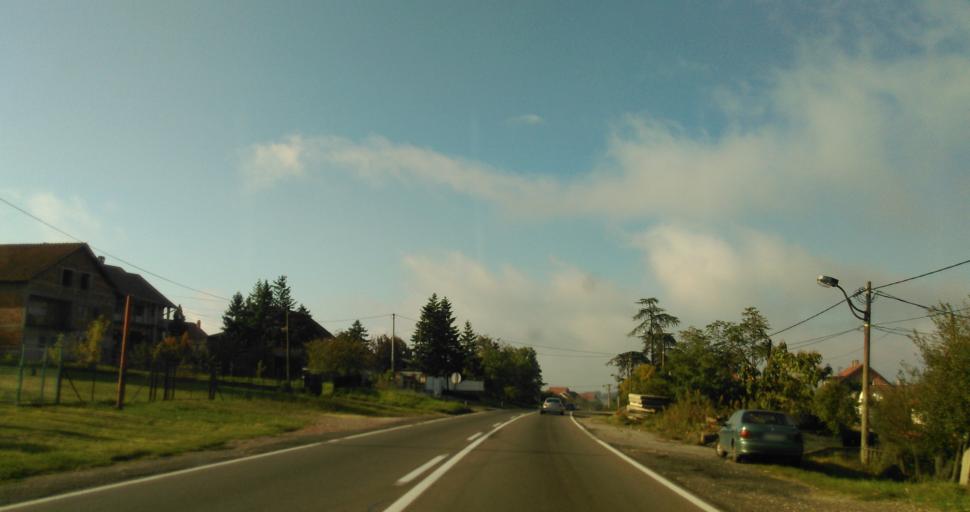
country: RS
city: Velika Mostanica
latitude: 44.6289
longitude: 20.3784
